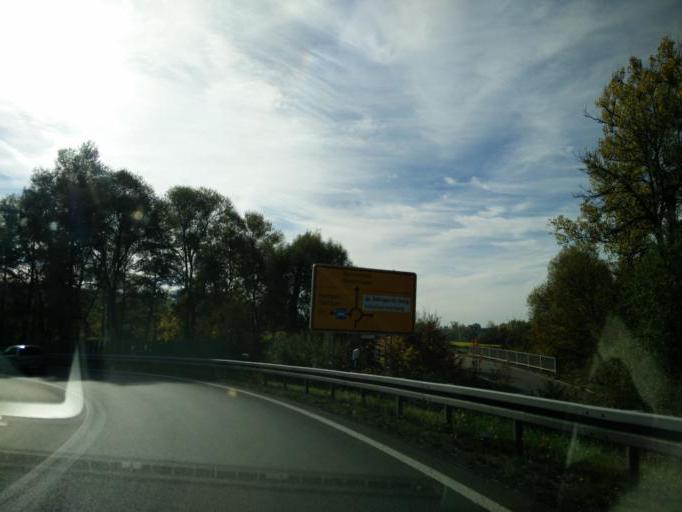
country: DE
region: Baden-Wuerttemberg
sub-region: Tuebingen Region
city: Dusslingen
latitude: 48.4715
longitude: 9.0642
